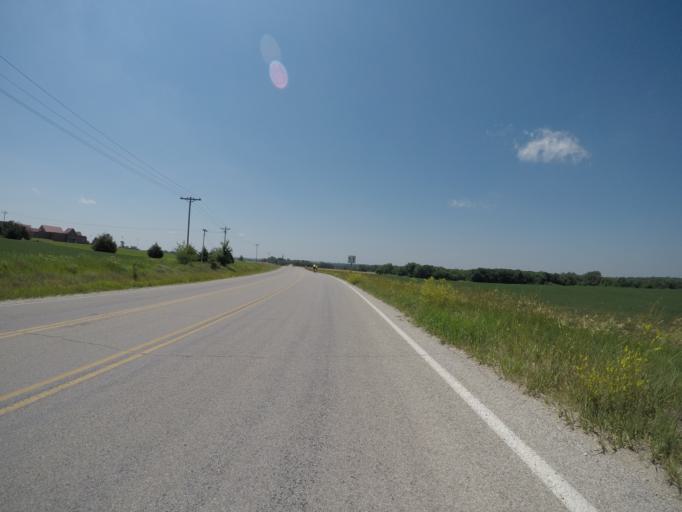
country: US
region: Kansas
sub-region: Pottawatomie County
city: Westmoreland
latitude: 39.3039
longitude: -96.4408
